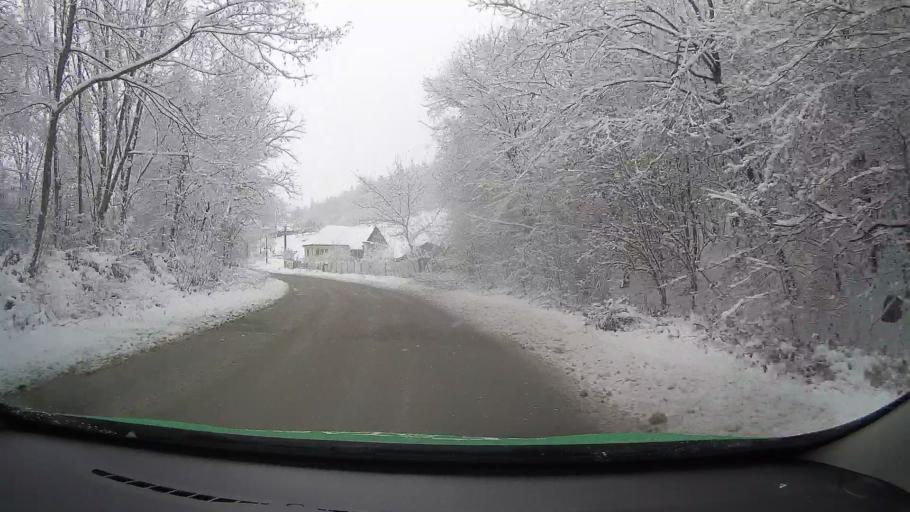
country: RO
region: Hunedoara
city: Hunedoara
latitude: 45.7388
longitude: 22.8818
